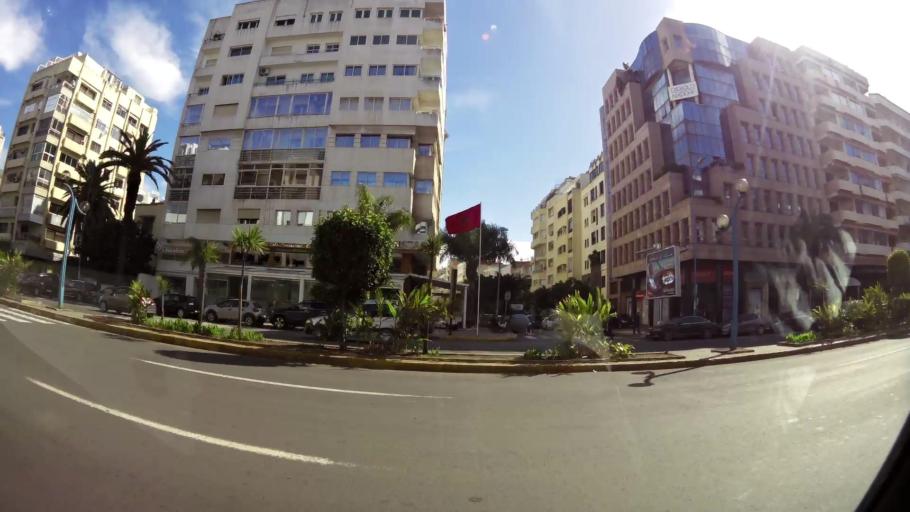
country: MA
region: Grand Casablanca
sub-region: Casablanca
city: Casablanca
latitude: 33.5891
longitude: -7.6336
